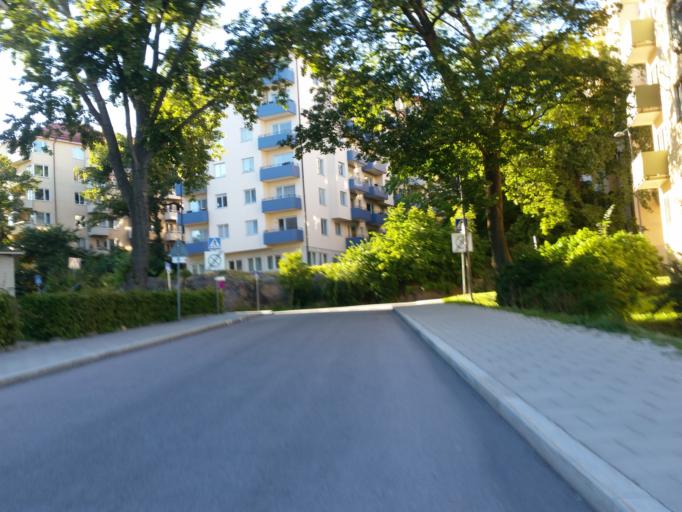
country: SE
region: Stockholm
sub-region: Solna Kommun
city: Solna
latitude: 59.3234
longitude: 18.0073
